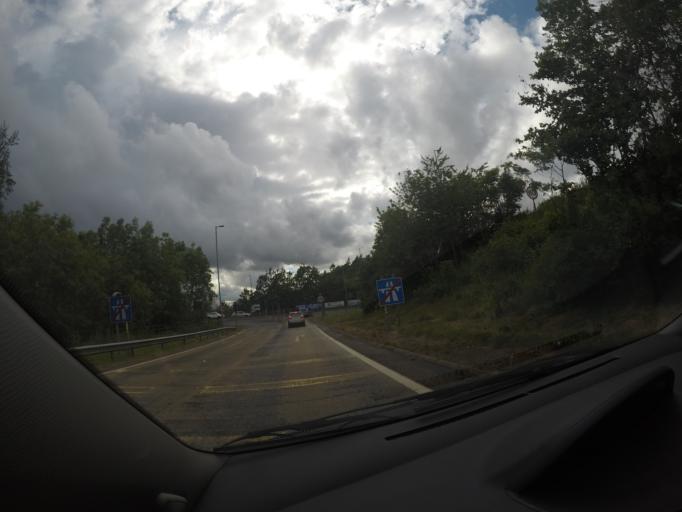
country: GB
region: Scotland
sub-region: North Lanarkshire
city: Stepps
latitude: 55.8349
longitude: -4.1587
